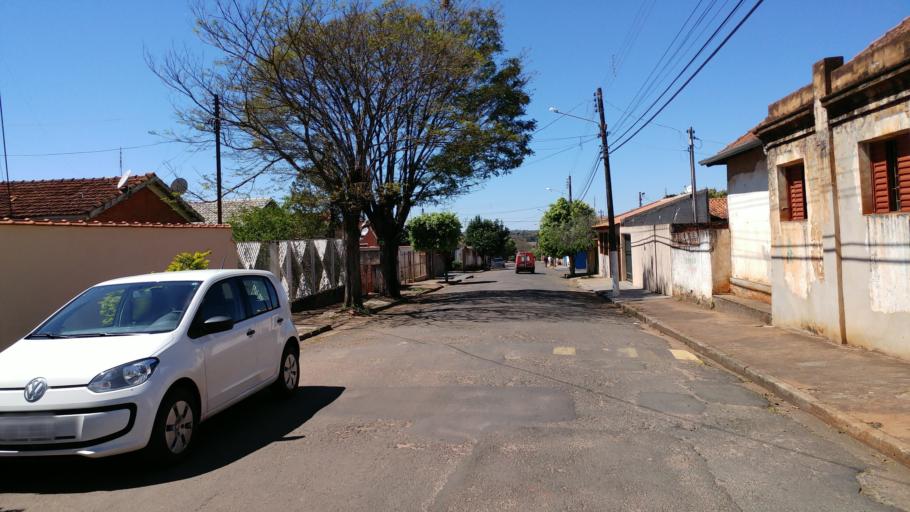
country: BR
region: Sao Paulo
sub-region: Paraguacu Paulista
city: Paraguacu Paulista
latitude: -22.4127
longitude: -50.5697
